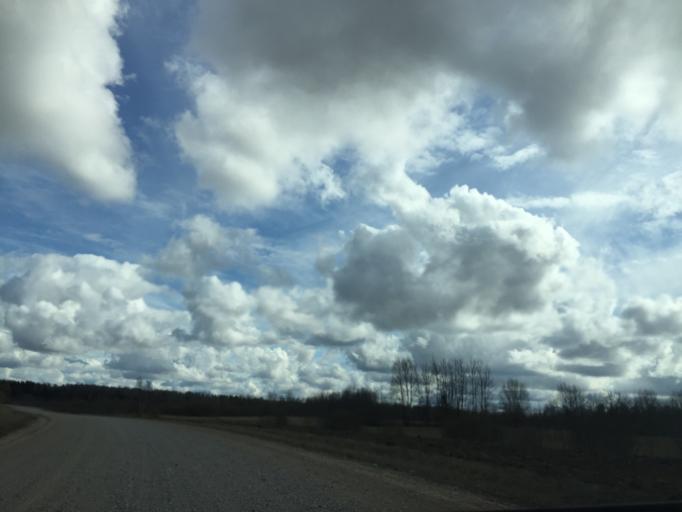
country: LV
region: Limbazu Rajons
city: Limbazi
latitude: 57.6140
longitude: 24.7792
